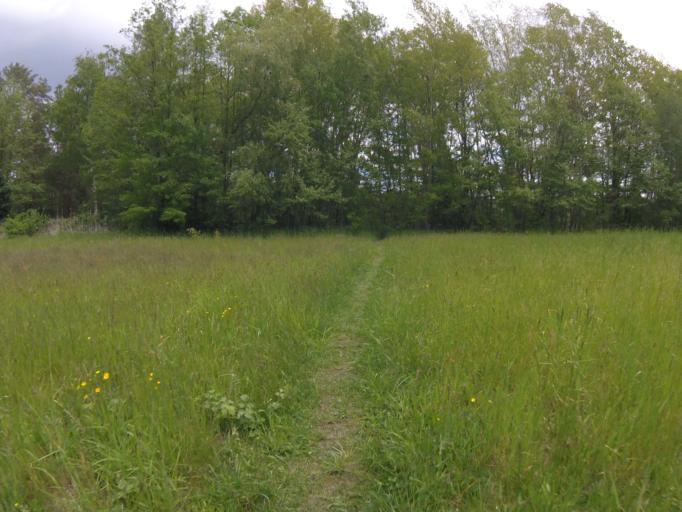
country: DE
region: Brandenburg
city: Bestensee
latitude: 52.2593
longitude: 13.6674
